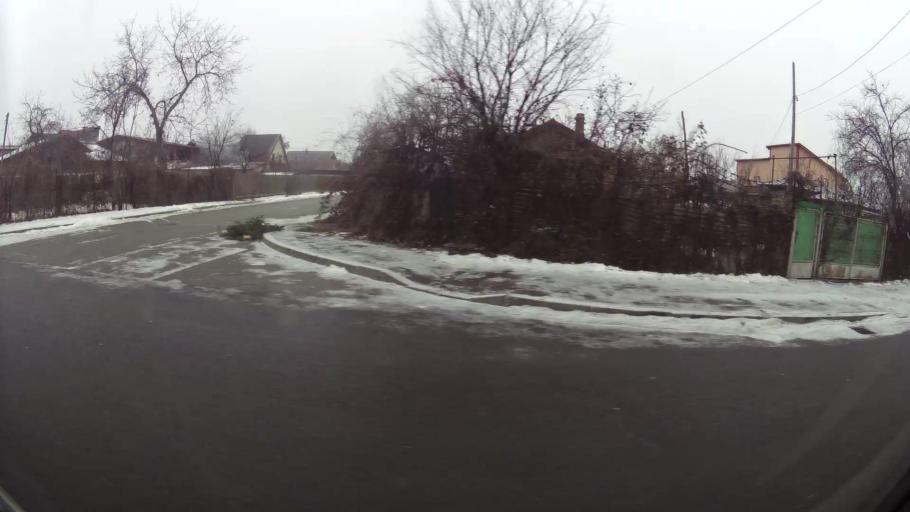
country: RO
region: Prahova
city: Ploiesti
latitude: 44.9539
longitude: 26.0428
